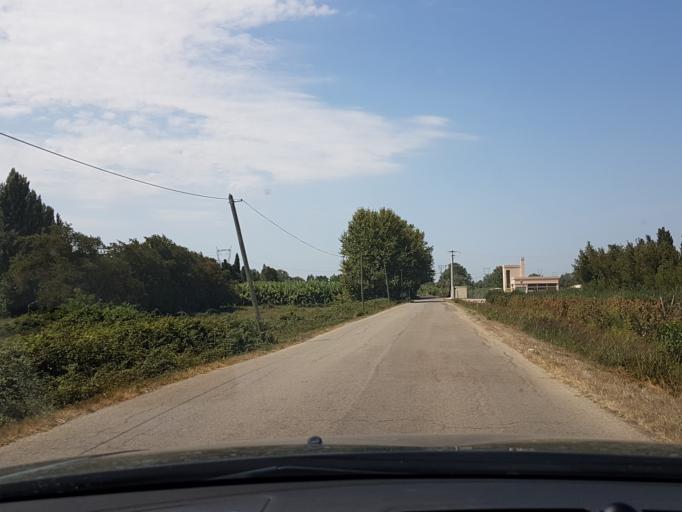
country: FR
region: Provence-Alpes-Cote d'Azur
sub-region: Departement des Bouches-du-Rhone
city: Molleges
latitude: 43.8043
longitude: 4.9000
